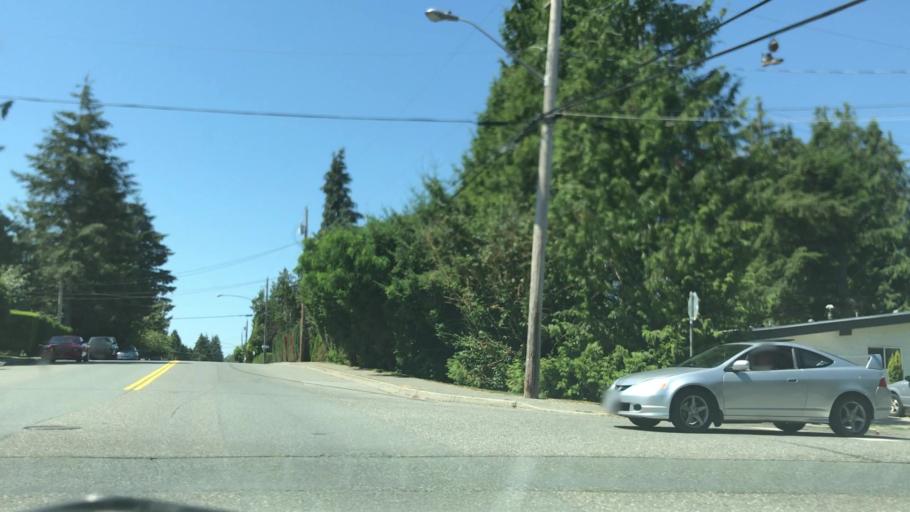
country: CA
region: British Columbia
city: Aldergrove
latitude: 49.0555
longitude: -122.4837
